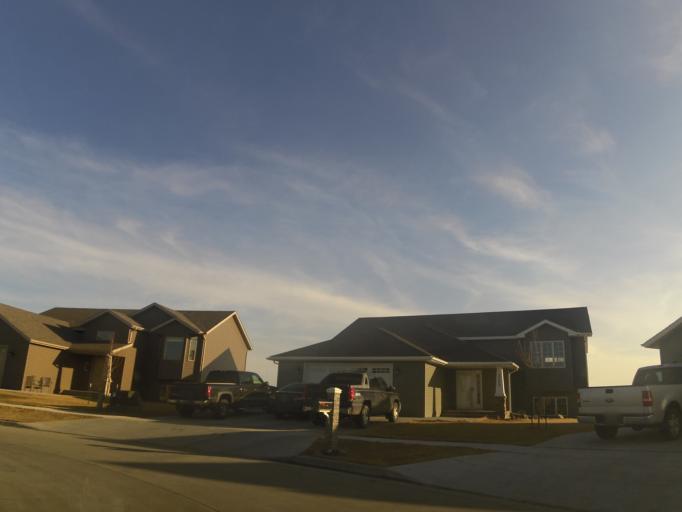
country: US
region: North Dakota
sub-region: Grand Forks County
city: Grand Forks
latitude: 47.8669
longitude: -97.0396
